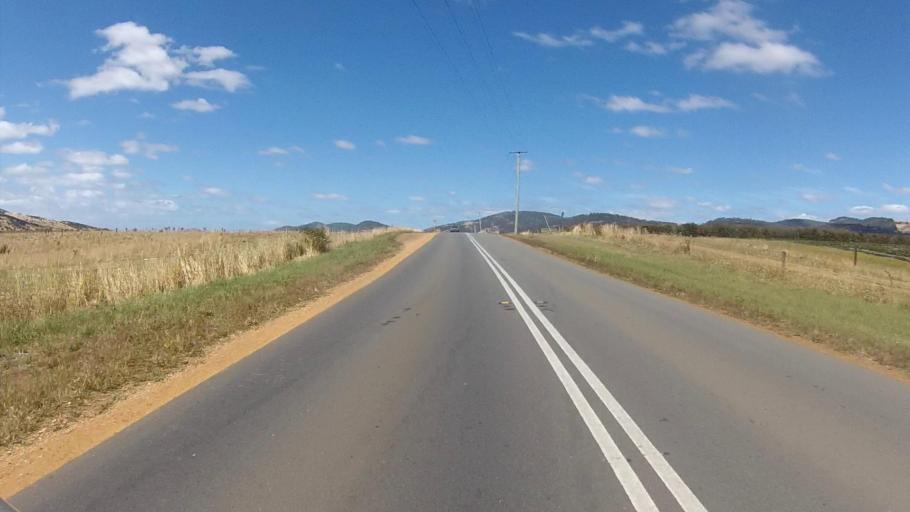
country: AU
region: Tasmania
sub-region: Clarence
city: Cambridge
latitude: -42.7559
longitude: 147.4156
